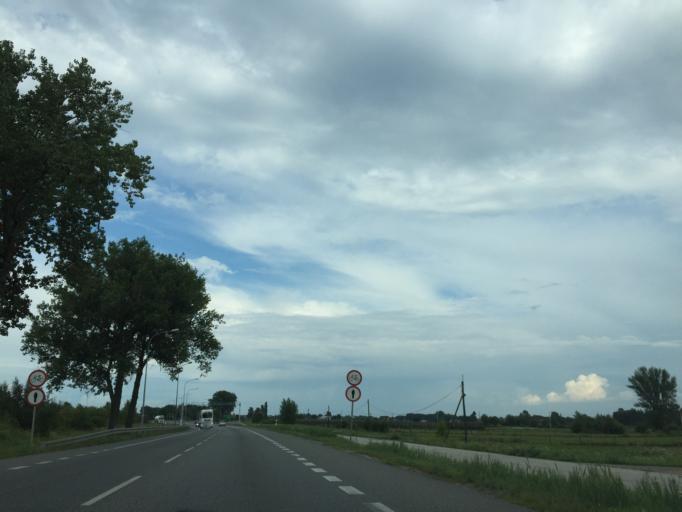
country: PL
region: Masovian Voivodeship
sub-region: Powiat piaseczynski
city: Prazmow
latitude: 51.8931
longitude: 20.9849
